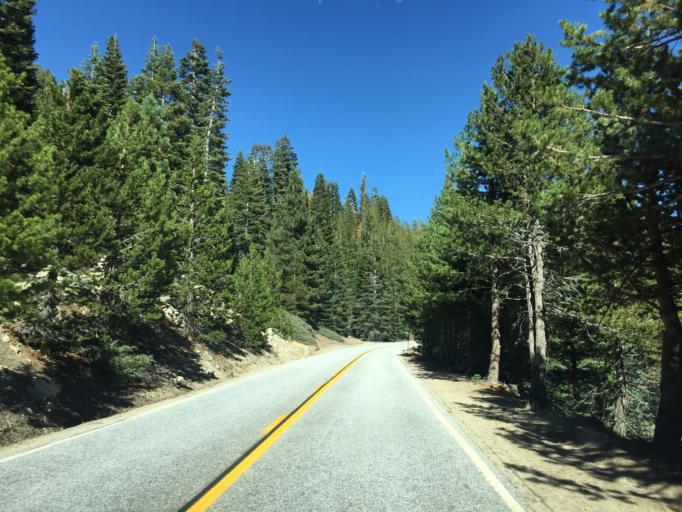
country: US
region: California
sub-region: Mariposa County
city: Yosemite Valley
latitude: 37.8108
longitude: -119.5331
